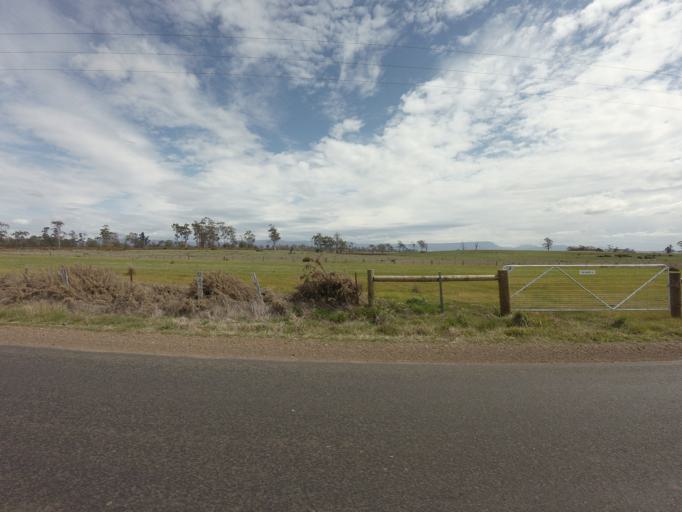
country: AU
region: Tasmania
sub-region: Northern Midlands
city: Longford
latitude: -41.7265
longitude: 147.1922
